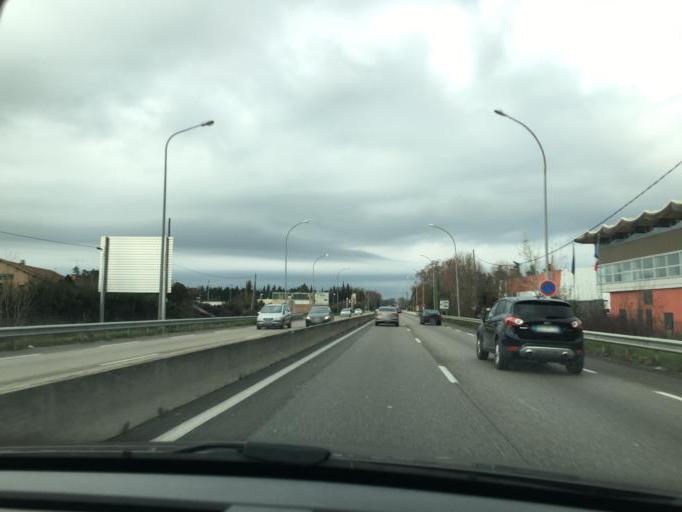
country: FR
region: Provence-Alpes-Cote d'Azur
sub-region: Departement des Bouches-du-Rhone
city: Noves
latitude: 43.9051
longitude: 4.8924
